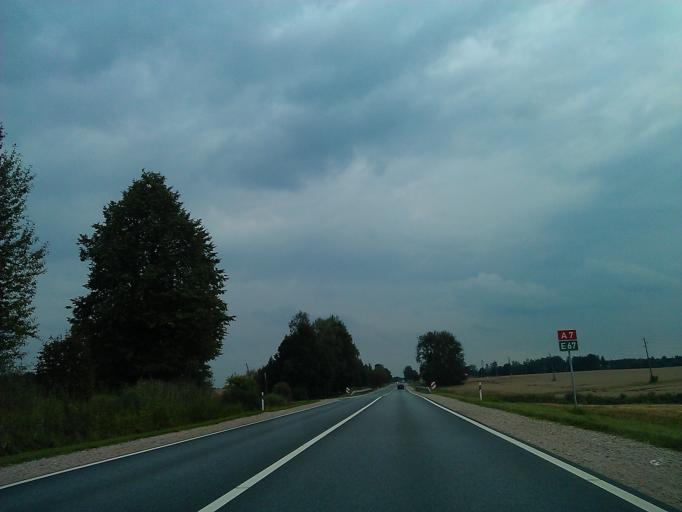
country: LV
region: Bauskas Rajons
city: Bauska
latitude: 56.5006
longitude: 24.1745
